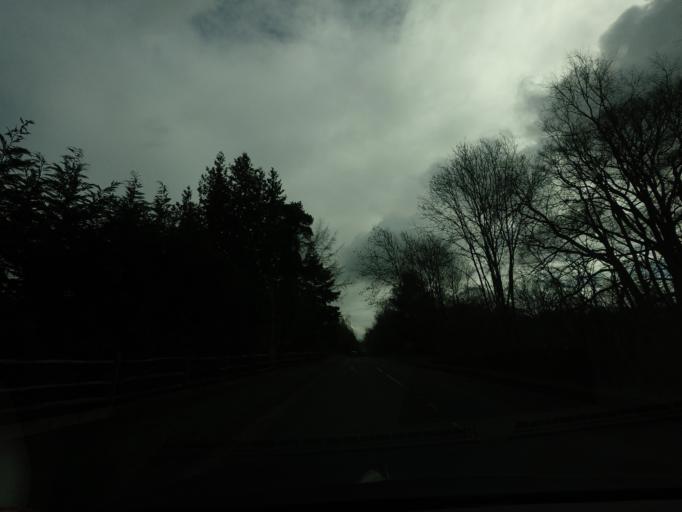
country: GB
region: England
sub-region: Kent
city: Kemsing
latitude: 51.2808
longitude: 0.2532
